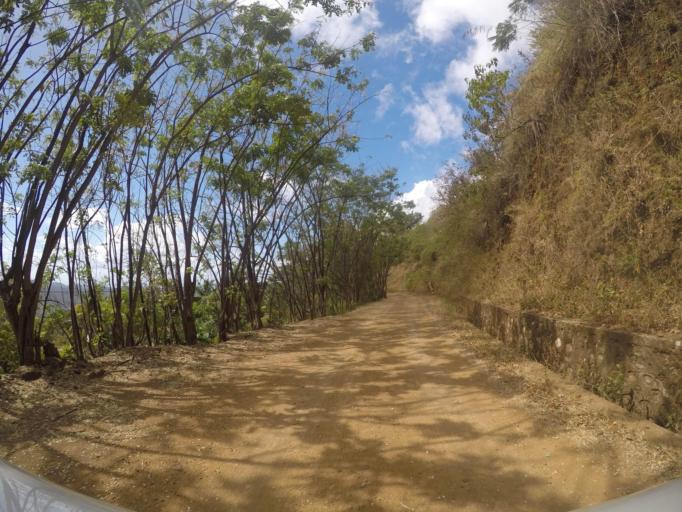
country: TL
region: Lautem
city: Lospalos
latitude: -8.5394
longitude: 126.8104
